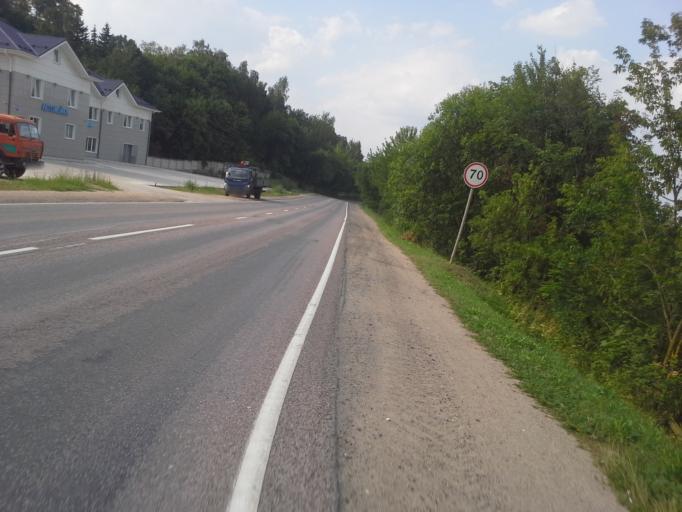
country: RU
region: Moskovskaya
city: Istra
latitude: 55.9012
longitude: 36.8083
